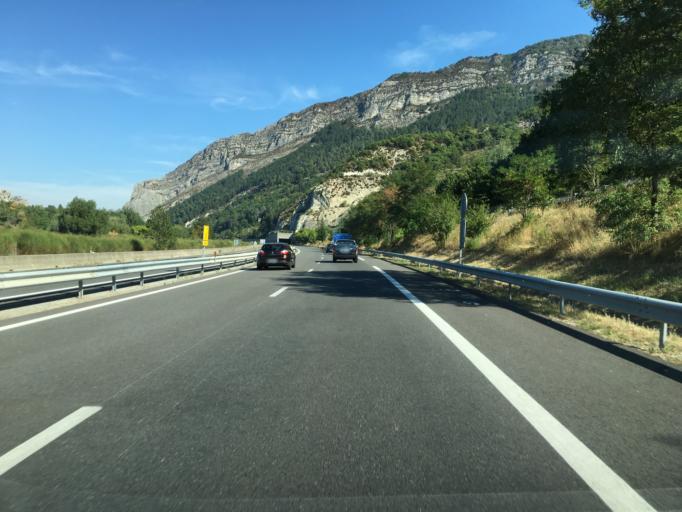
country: FR
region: Provence-Alpes-Cote d'Azur
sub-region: Departement des Alpes-de-Haute-Provence
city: Sisteron
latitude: 44.1870
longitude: 5.9556
